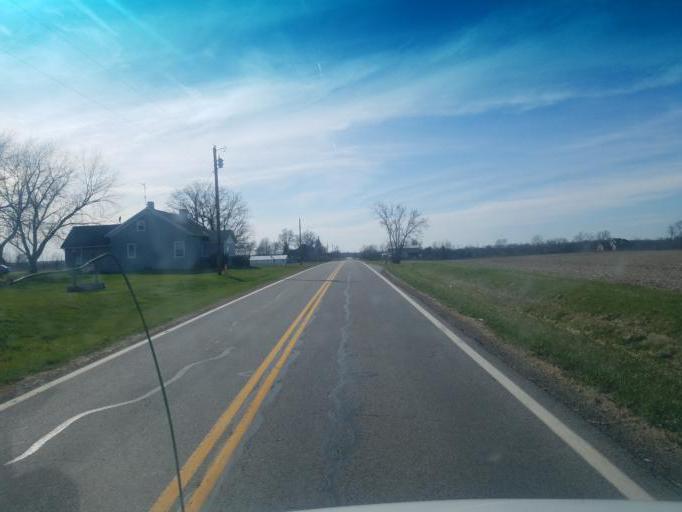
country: US
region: Ohio
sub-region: Champaign County
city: North Lewisburg
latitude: 40.3457
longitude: -83.5009
